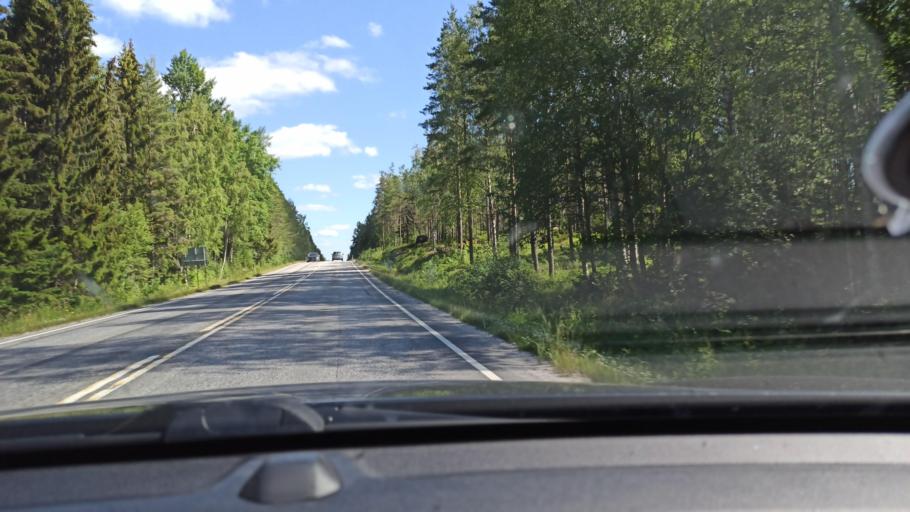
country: FI
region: Ostrobothnia
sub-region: Vaasa
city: Malax
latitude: 62.9869
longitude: 21.6349
